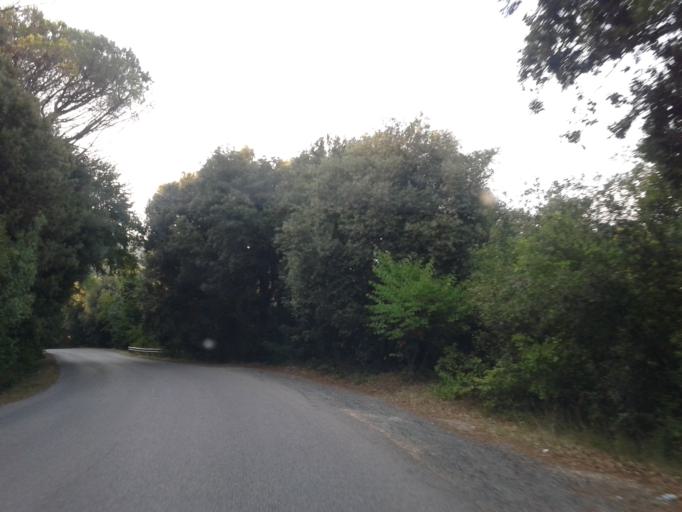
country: IT
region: Tuscany
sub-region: Provincia di Livorno
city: Rosignano Marittimo
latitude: 43.4012
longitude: 10.4899
